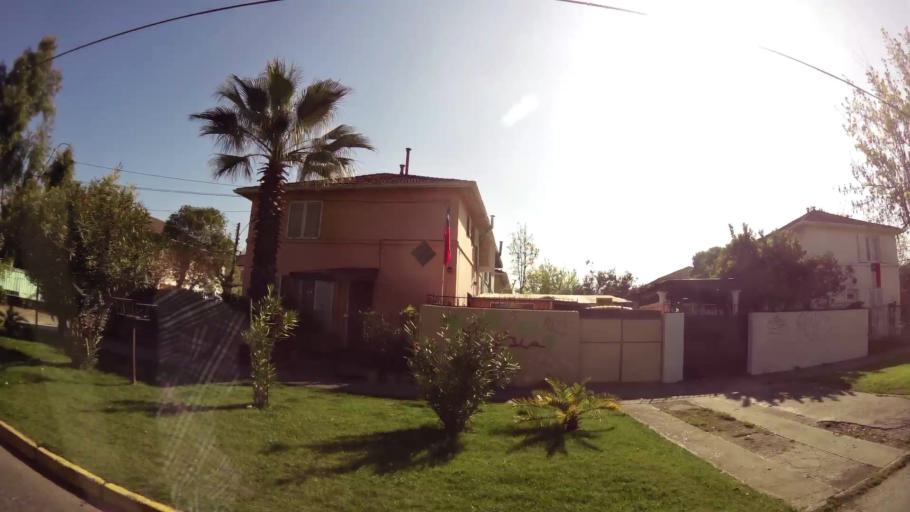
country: CL
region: Santiago Metropolitan
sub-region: Provincia de Santiago
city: Villa Presidente Frei, Nunoa, Santiago, Chile
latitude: -33.4397
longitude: -70.5866
